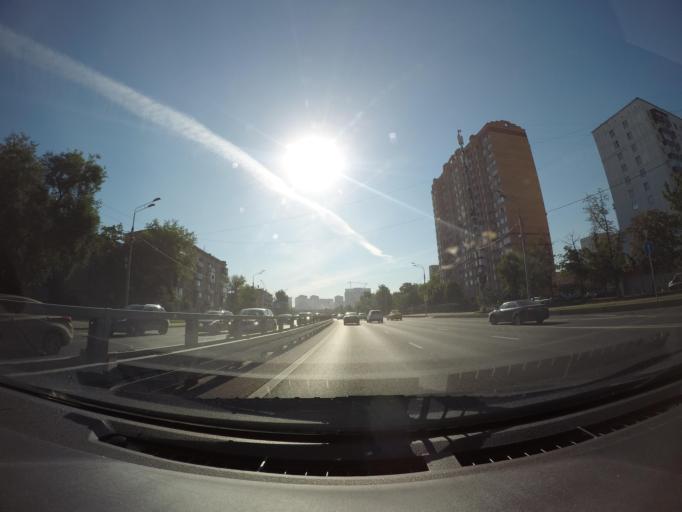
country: RU
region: Moscow
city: Lefortovo
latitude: 55.7320
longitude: 37.7174
